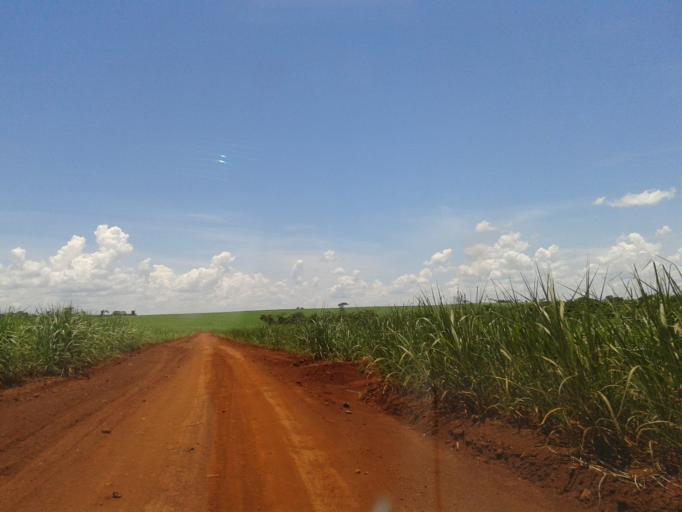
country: BR
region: Minas Gerais
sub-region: Centralina
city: Centralina
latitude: -18.6182
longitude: -49.2788
